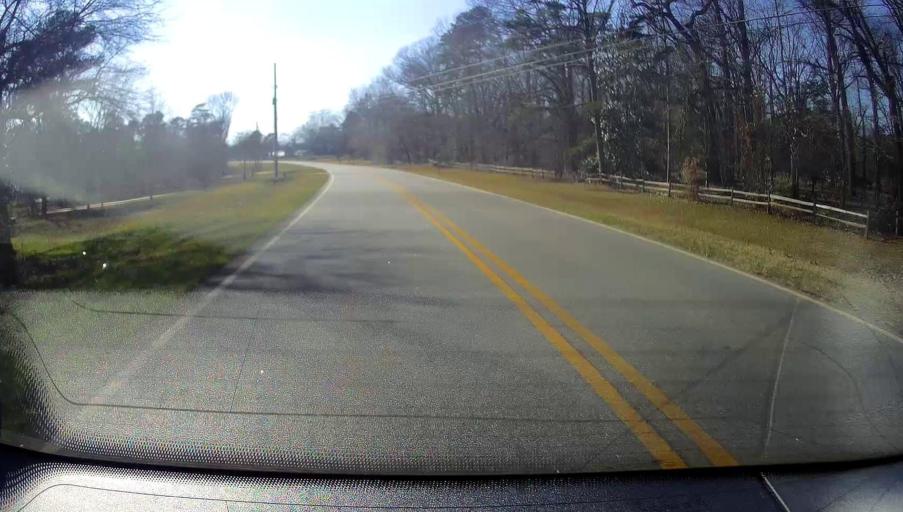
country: US
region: Georgia
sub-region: Monroe County
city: Forsyth
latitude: 33.0442
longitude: -83.9119
